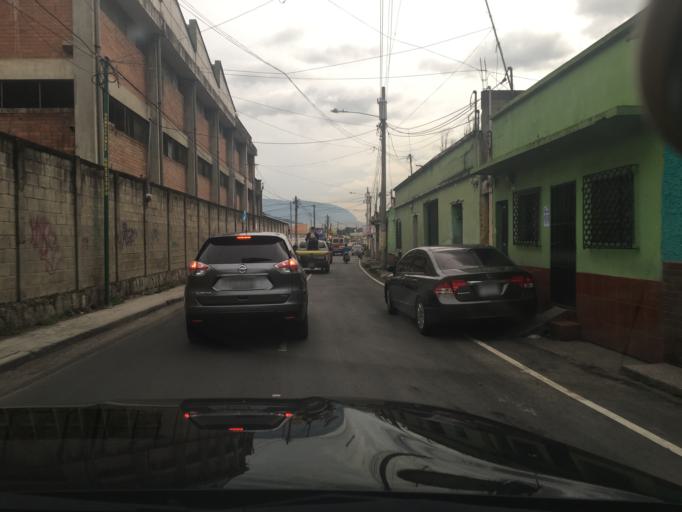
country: GT
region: Guatemala
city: Amatitlan
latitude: 14.4836
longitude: -90.6163
